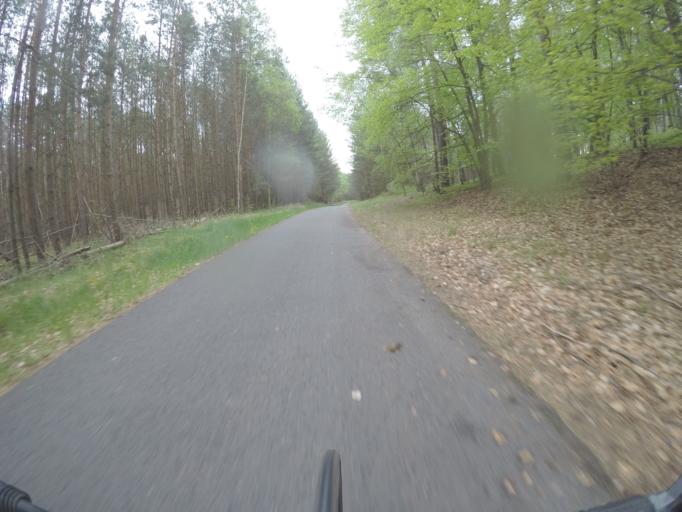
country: DE
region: Brandenburg
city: Biesenthal
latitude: 52.7977
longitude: 13.6259
